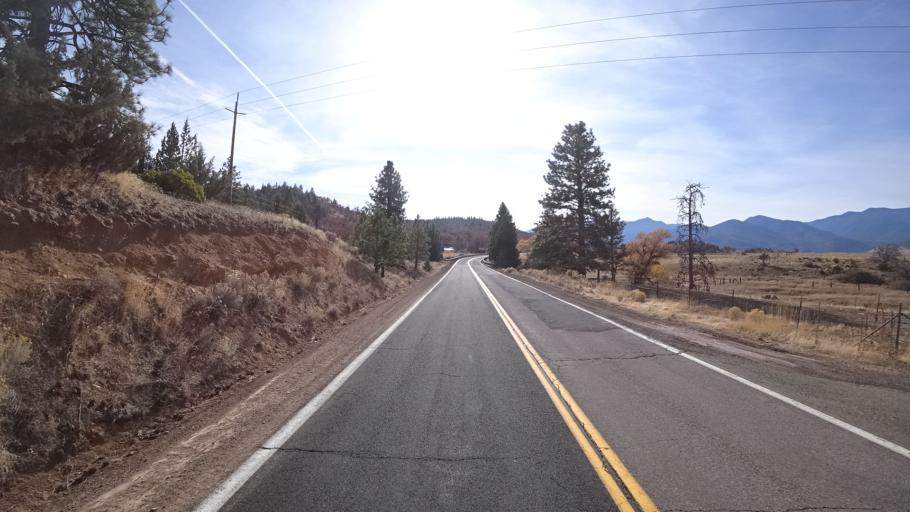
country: US
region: California
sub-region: Siskiyou County
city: Weed
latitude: 41.4701
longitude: -122.4139
